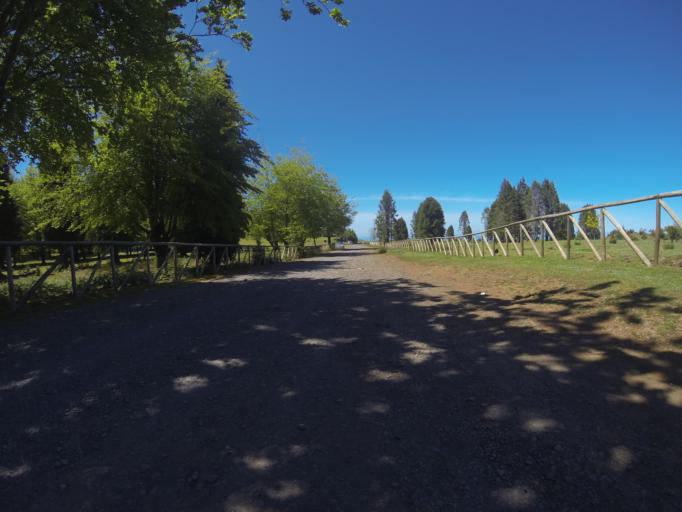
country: PT
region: Madeira
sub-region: Funchal
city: Nossa Senhora do Monte
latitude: 32.7244
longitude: -16.8866
